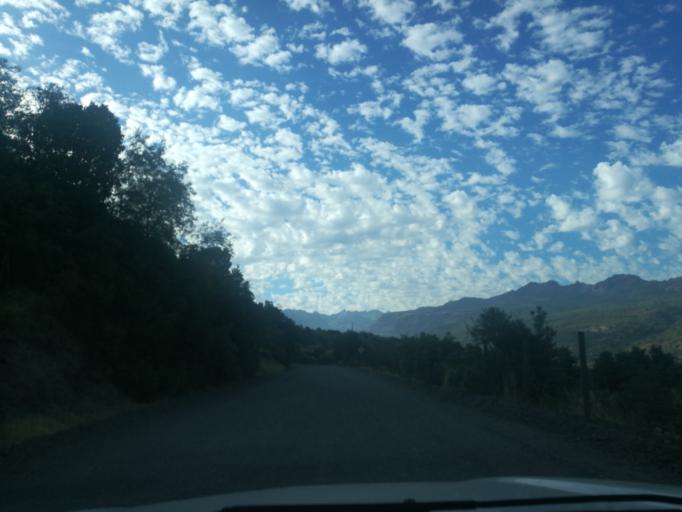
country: CL
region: O'Higgins
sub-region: Provincia de Cachapoal
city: Machali
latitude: -34.2477
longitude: -70.4677
